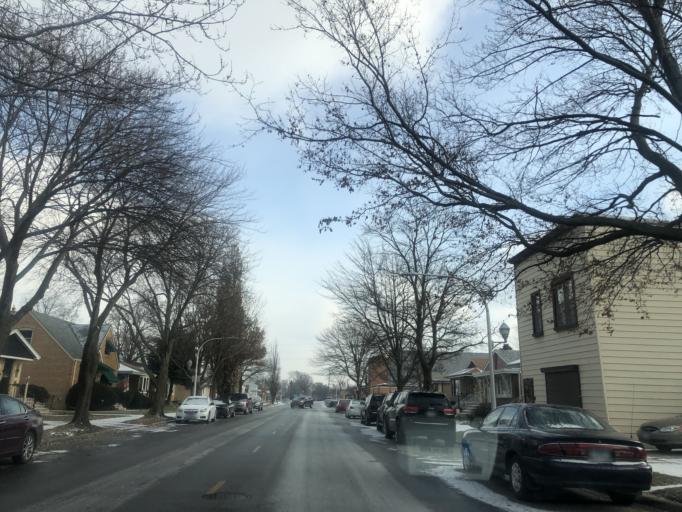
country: US
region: Illinois
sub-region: Cook County
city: Hometown
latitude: 41.7423
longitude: -87.7156
